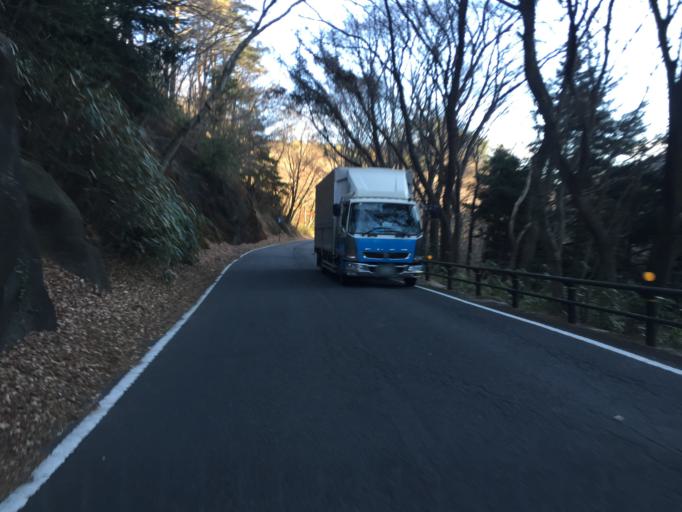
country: JP
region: Fukushima
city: Iwaki
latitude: 37.1892
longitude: 140.8148
